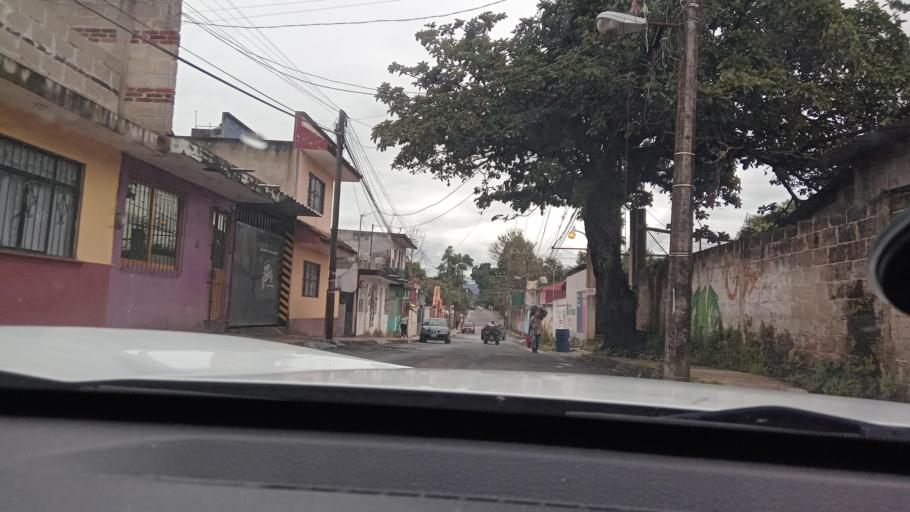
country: MX
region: Veracruz
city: Coatepec
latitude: 19.4462
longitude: -96.9693
